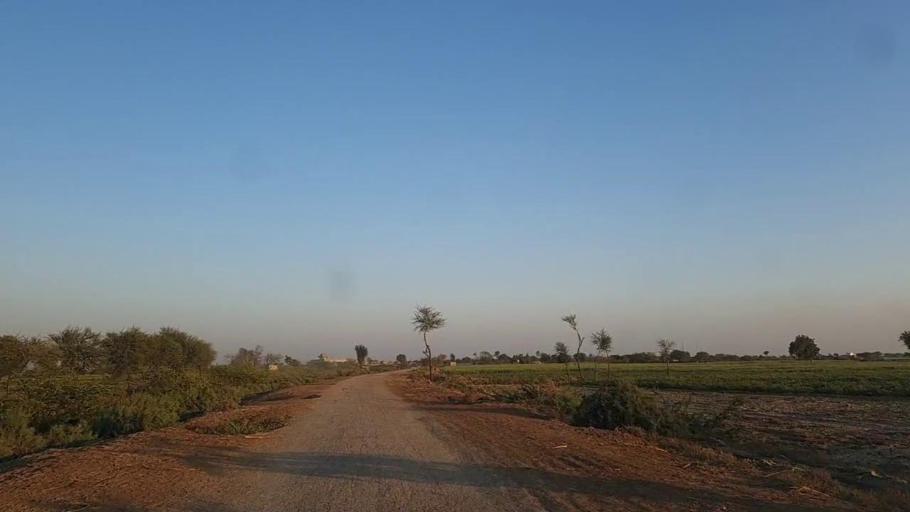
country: PK
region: Sindh
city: Samaro
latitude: 25.2997
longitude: 69.3806
